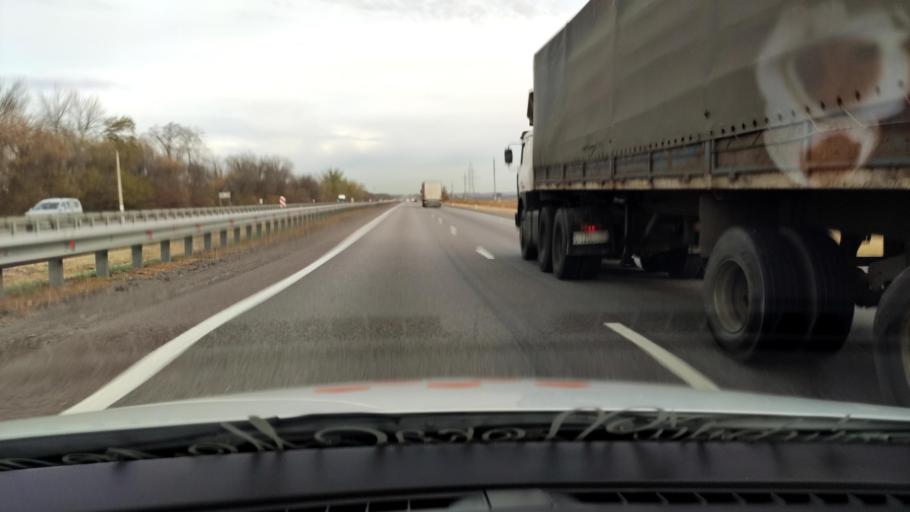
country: RU
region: Voronezj
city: Ramon'
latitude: 51.9085
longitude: 39.2193
